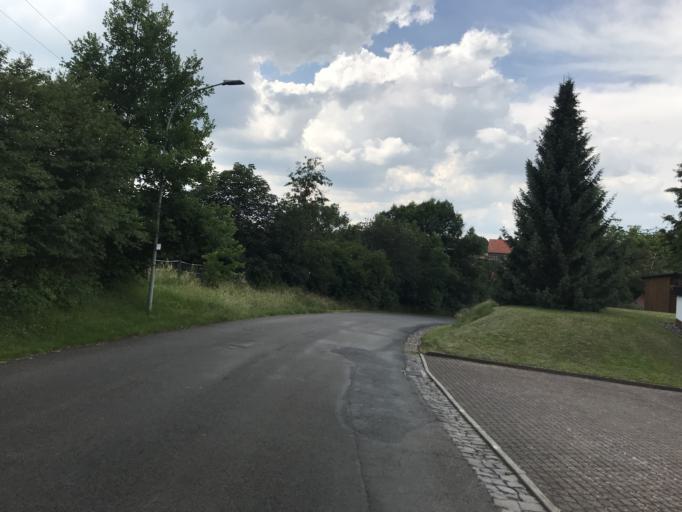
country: DE
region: Hesse
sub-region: Regierungsbezirk Giessen
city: Laubach
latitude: 50.5156
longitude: 8.9623
